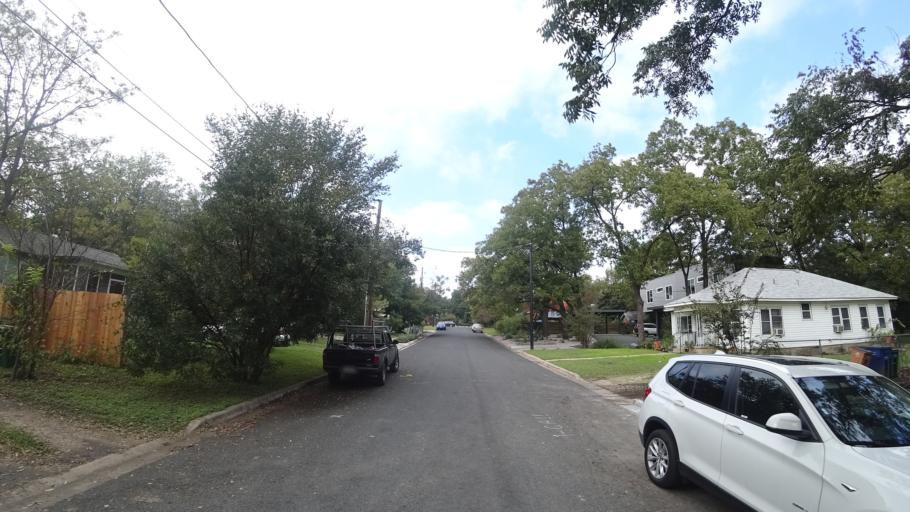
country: US
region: Texas
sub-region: Travis County
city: Austin
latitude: 30.2488
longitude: -97.7572
